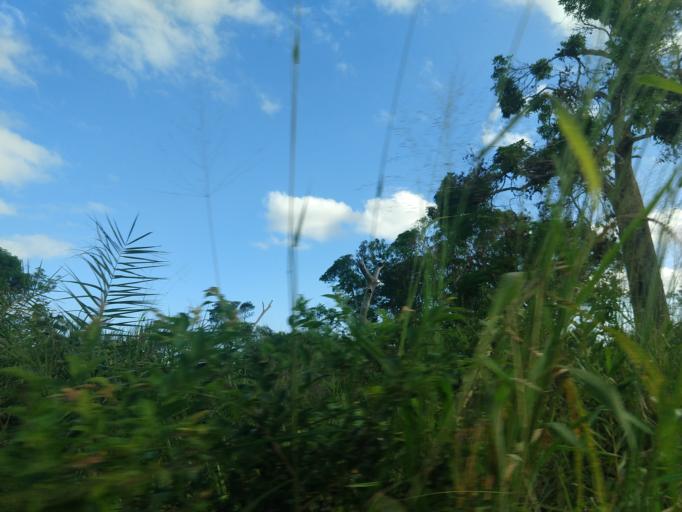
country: MZ
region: Sofala
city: Beira
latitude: -19.6040
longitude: 35.1406
